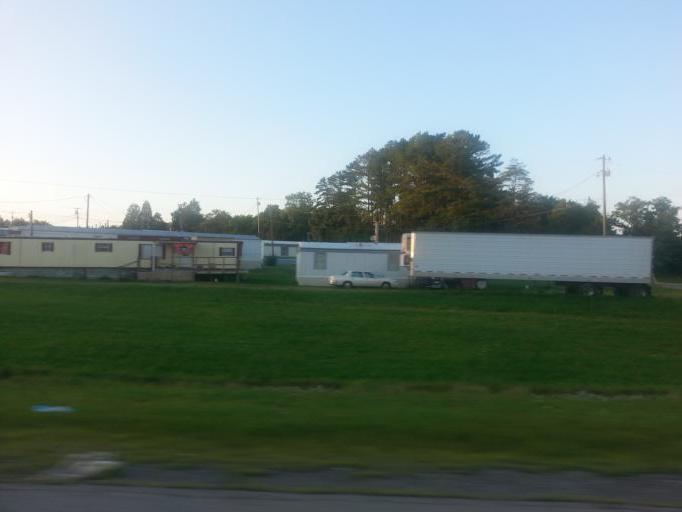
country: US
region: Tennessee
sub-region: Knox County
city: Mascot
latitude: 36.0262
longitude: -83.7303
